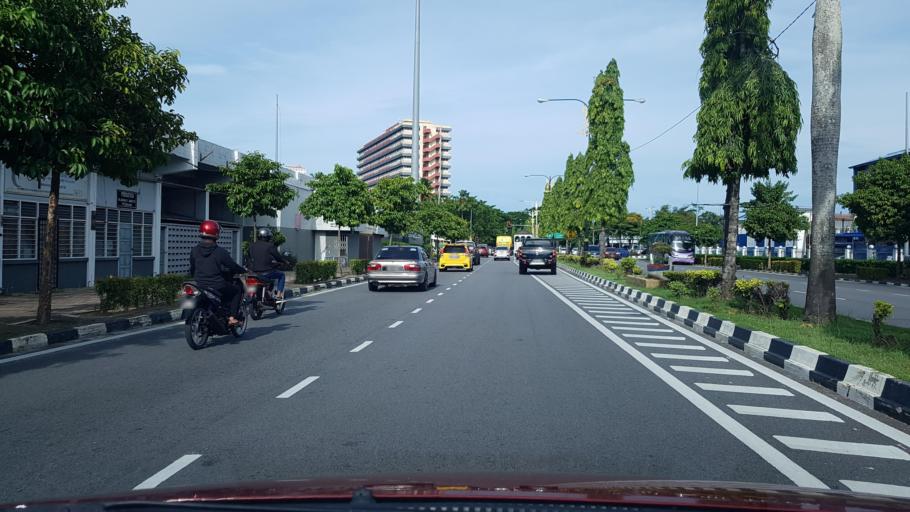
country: MY
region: Terengganu
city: Kuala Terengganu
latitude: 5.3288
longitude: 103.1399
